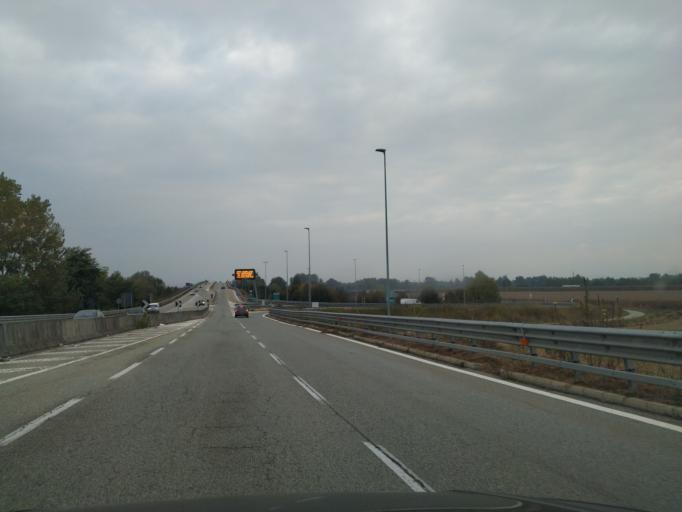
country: IT
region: Piedmont
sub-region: Provincia di Torino
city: Brandizzo
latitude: 45.1885
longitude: 7.8563
